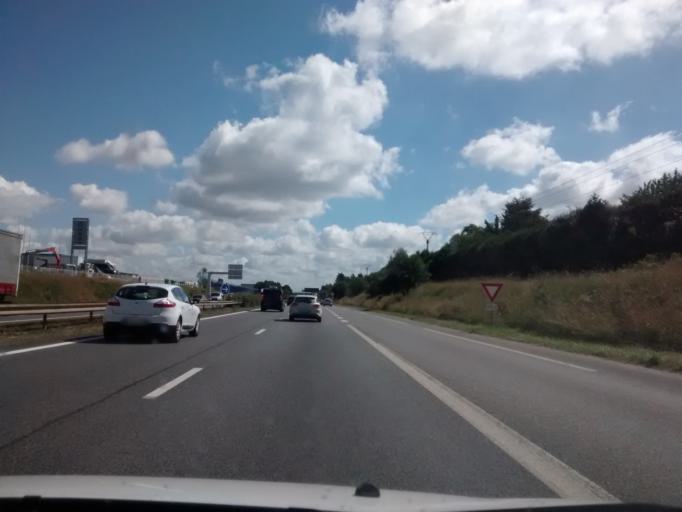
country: FR
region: Brittany
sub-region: Departement d'Ille-et-Vilaine
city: Chantepie
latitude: 48.0934
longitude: -1.6243
